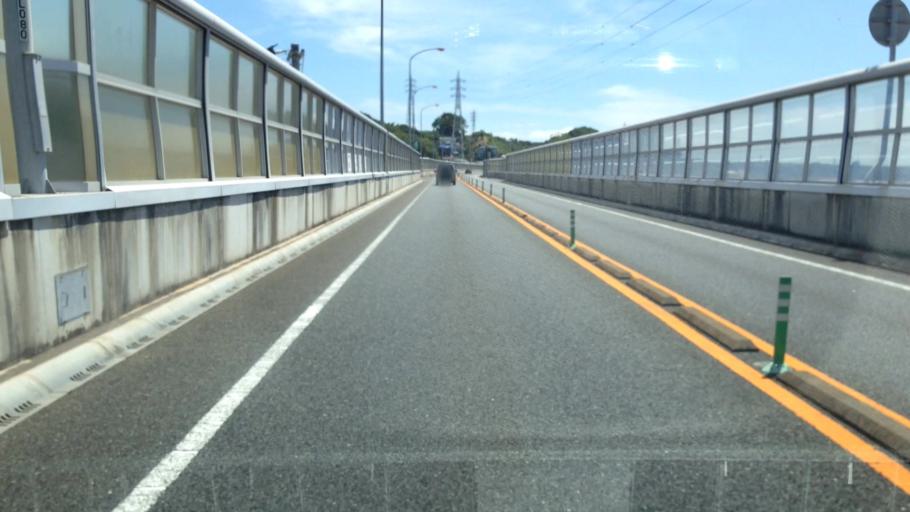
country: JP
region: Kanagawa
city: Yokosuka
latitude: 35.2199
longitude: 139.6371
